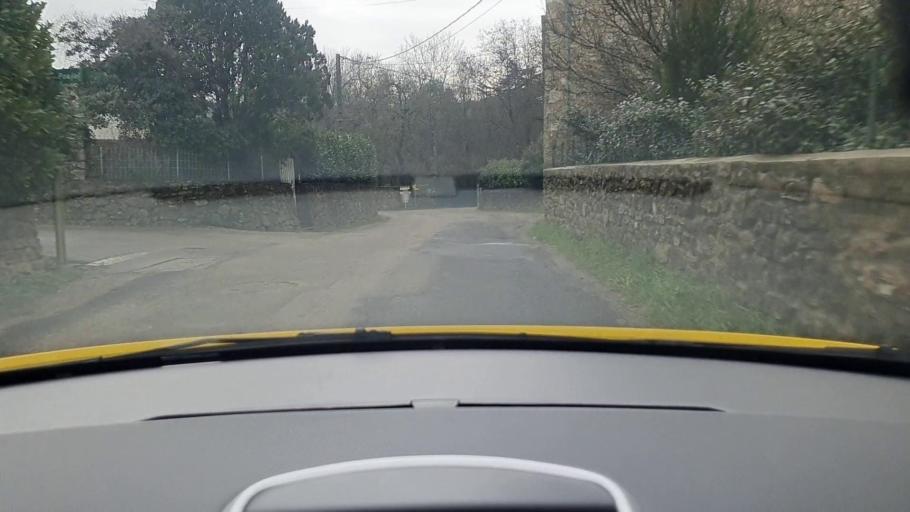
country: FR
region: Languedoc-Roussillon
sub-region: Departement du Gard
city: Besseges
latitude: 44.2750
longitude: 4.1238
